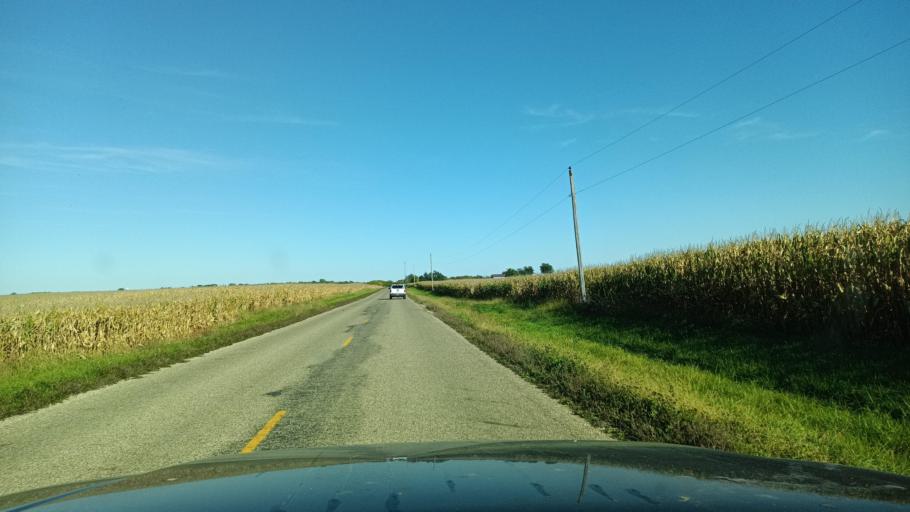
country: US
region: Illinois
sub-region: Logan County
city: Atlanta
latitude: 40.2344
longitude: -89.1467
